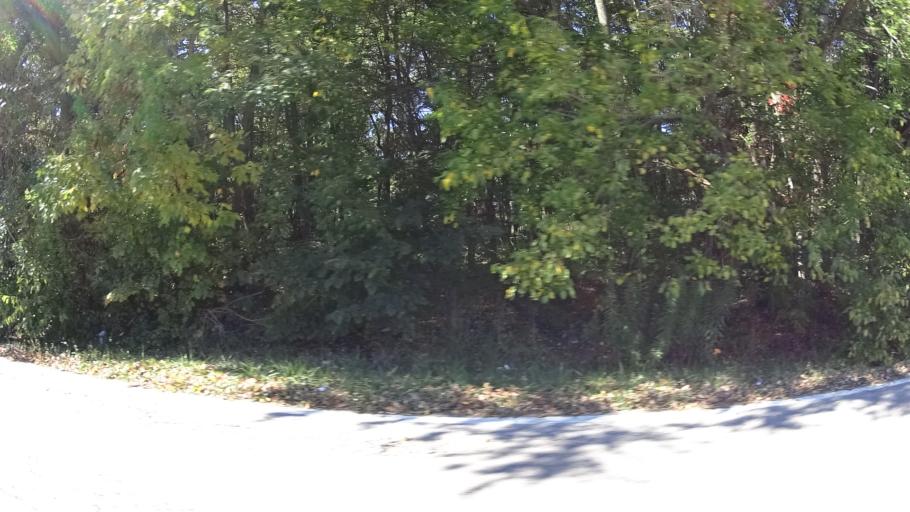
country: US
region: Ohio
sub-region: Lorain County
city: Amherst
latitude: 41.3982
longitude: -82.2506
